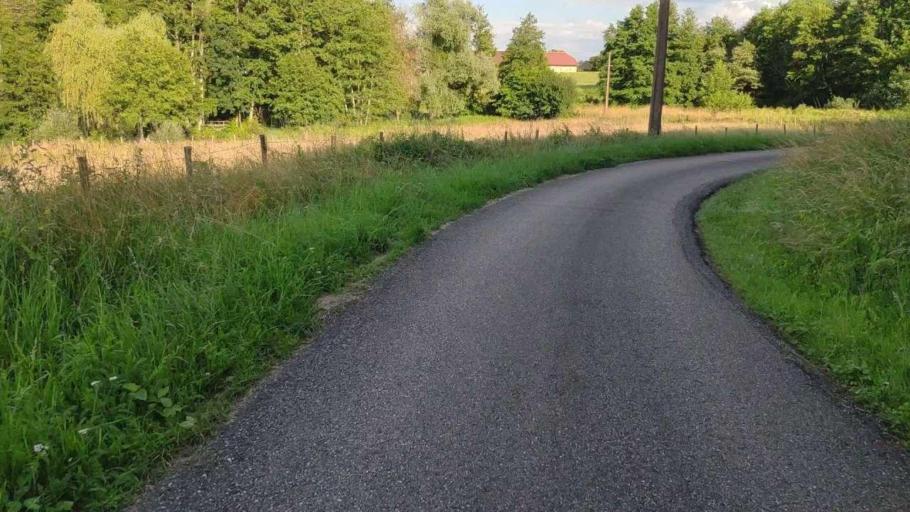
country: FR
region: Franche-Comte
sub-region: Departement du Jura
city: Bletterans
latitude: 46.7893
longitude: 5.4835
